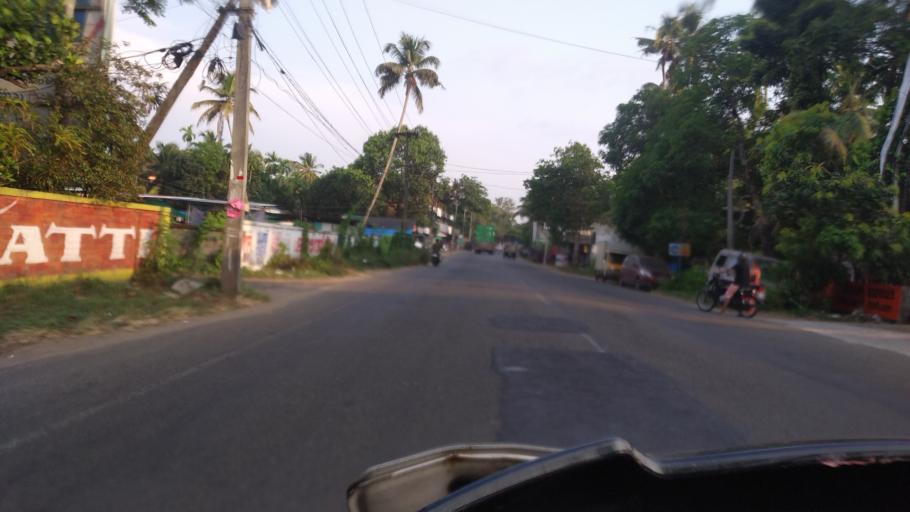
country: IN
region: Kerala
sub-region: Thrissur District
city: Irinjalakuda
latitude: 10.3283
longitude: 76.1423
